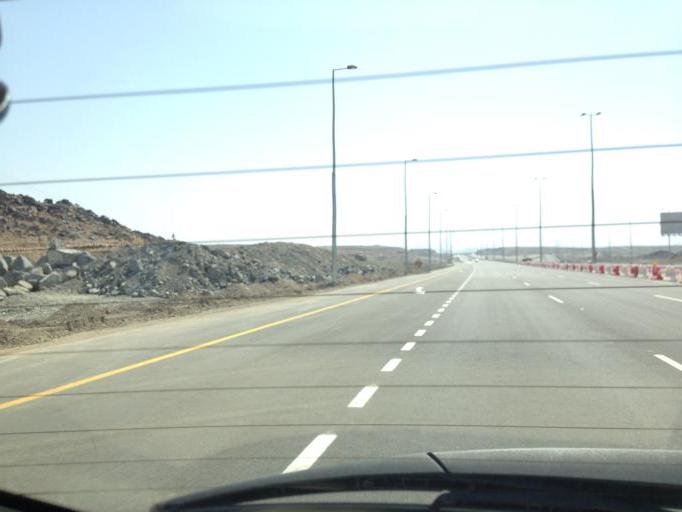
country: OM
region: Al Batinah
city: Rustaq
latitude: 23.5527
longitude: 57.5055
